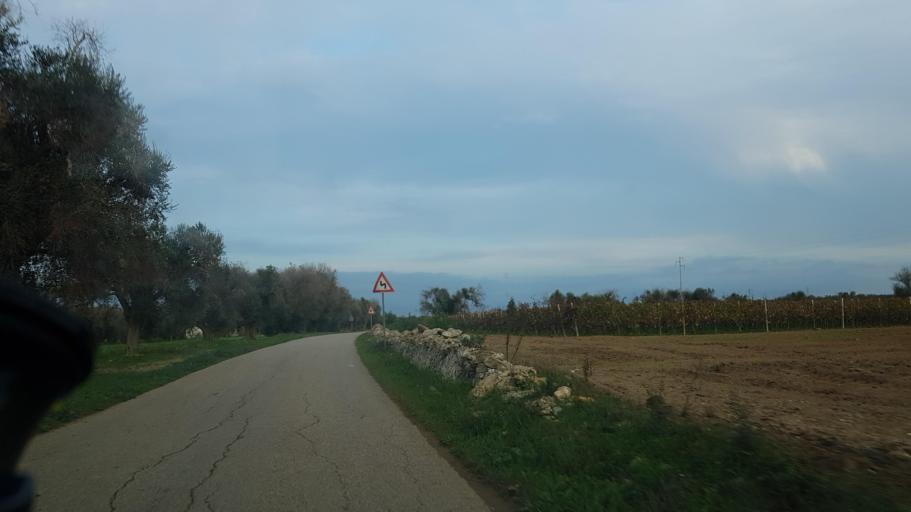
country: IT
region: Apulia
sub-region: Provincia di Brindisi
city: Latiano
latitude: 40.5390
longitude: 17.7434
